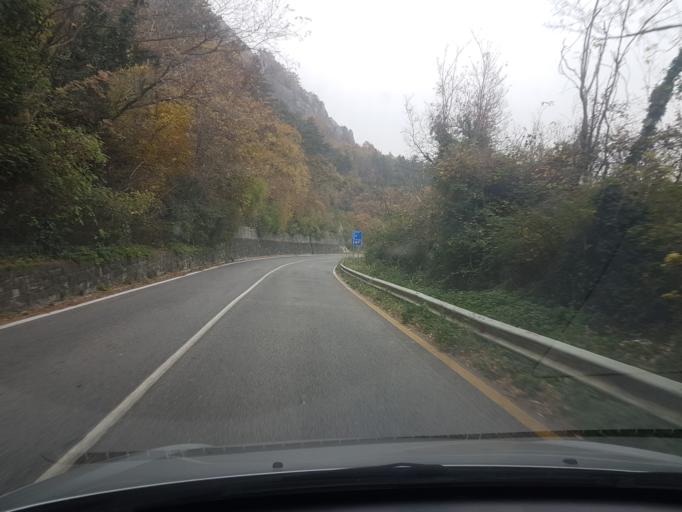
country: IT
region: Friuli Venezia Giulia
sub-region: Provincia di Trieste
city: Domio
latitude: 45.6309
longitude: 13.8422
